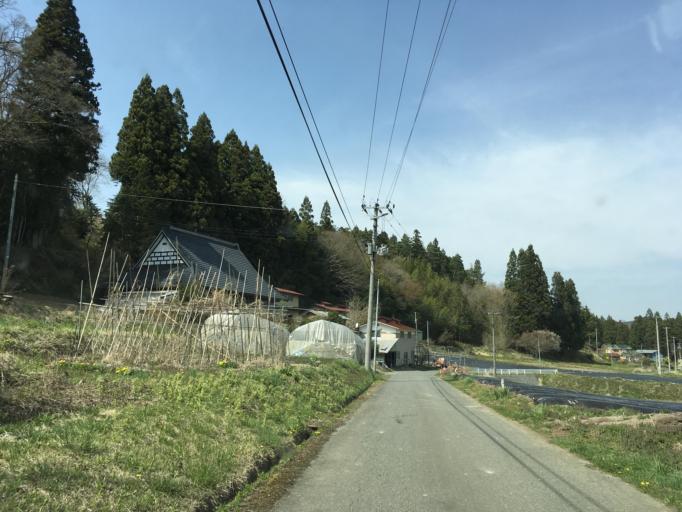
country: JP
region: Iwate
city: Ichinoseki
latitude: 38.8316
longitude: 141.3513
